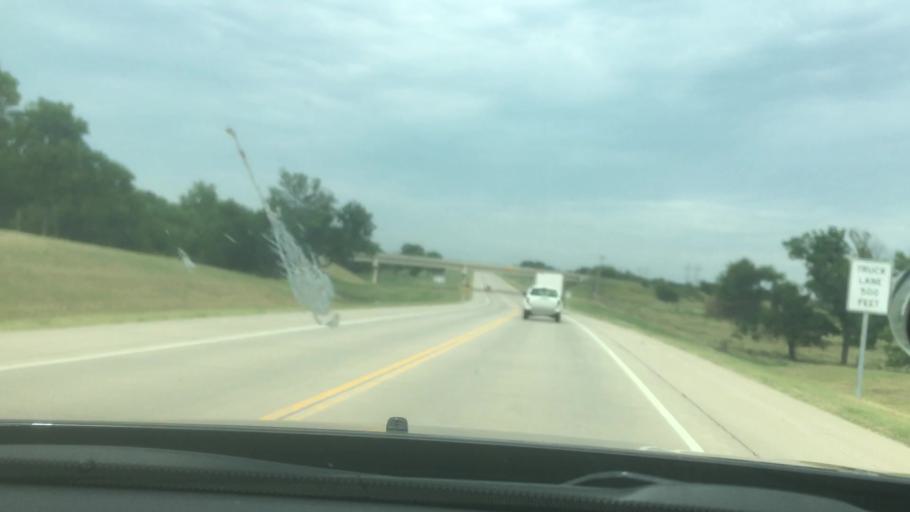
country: US
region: Oklahoma
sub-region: Murray County
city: Sulphur
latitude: 34.5913
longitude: -96.8976
